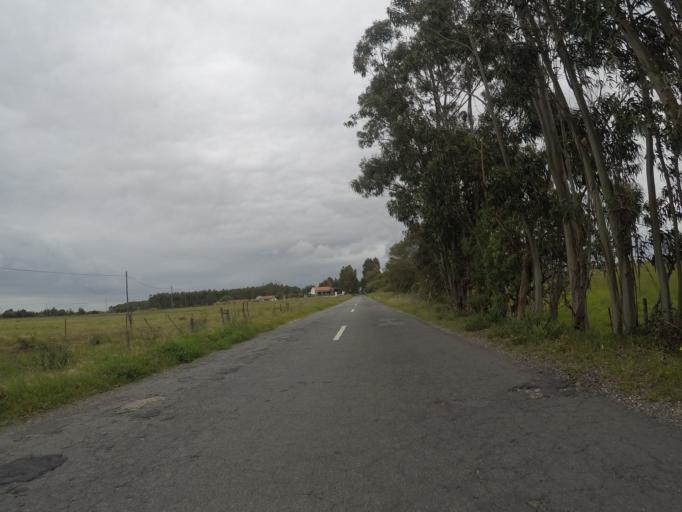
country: PT
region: Beja
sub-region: Odemira
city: Sao Teotonio
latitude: 37.5904
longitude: -8.7777
